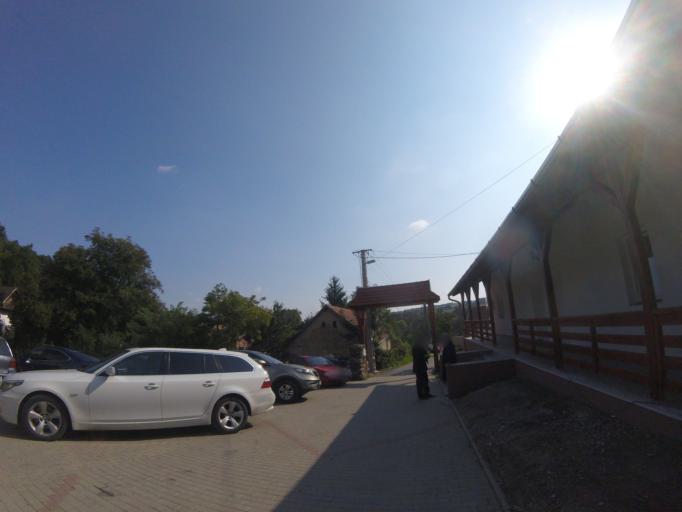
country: HU
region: Nograd
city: Bujak
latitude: 47.8673
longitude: 19.5023
